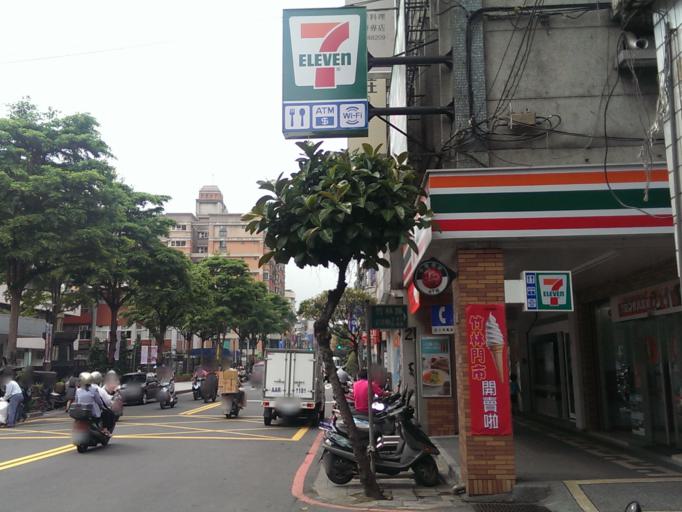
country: TW
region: Taipei
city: Taipei
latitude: 25.0088
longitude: 121.5206
